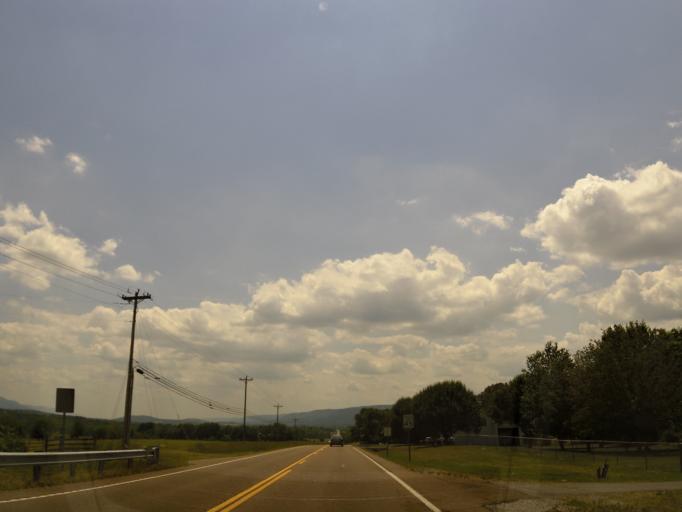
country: US
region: Tennessee
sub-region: Bledsoe County
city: Pikeville
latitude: 35.5920
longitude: -85.2020
